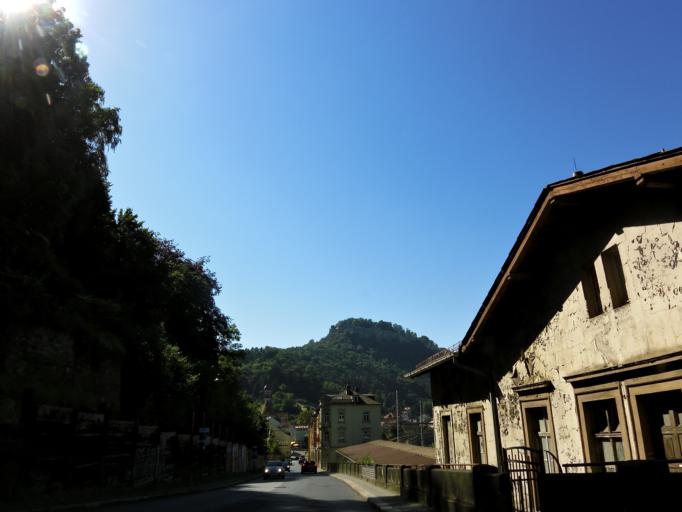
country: DE
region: Saxony
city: Konigstein
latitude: 50.9193
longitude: 14.0783
